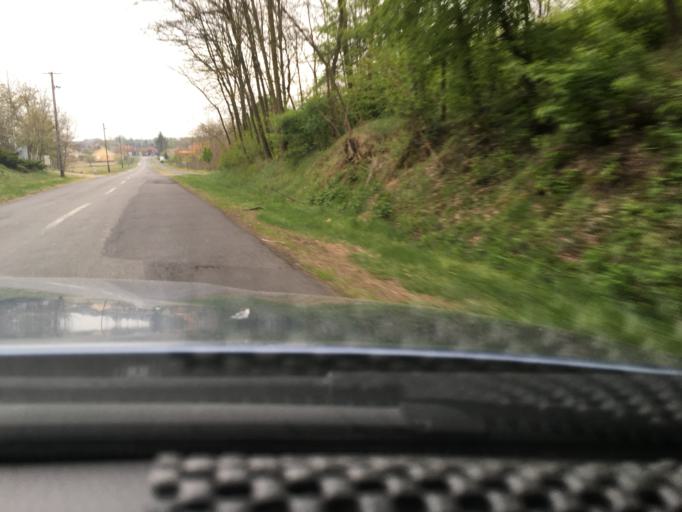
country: HU
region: Szabolcs-Szatmar-Bereg
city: Nyirlugos
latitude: 47.6926
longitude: 22.0284
